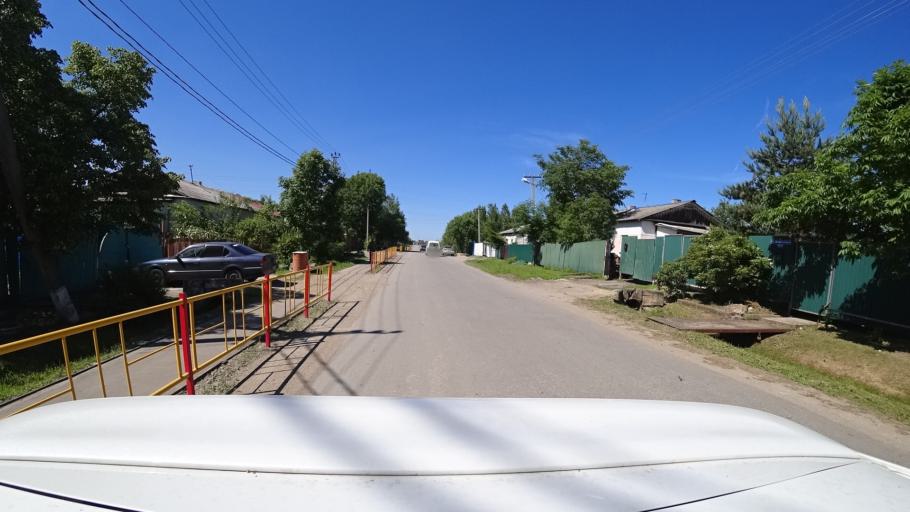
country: RU
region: Khabarovsk Krai
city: Topolevo
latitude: 48.5598
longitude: 135.1927
